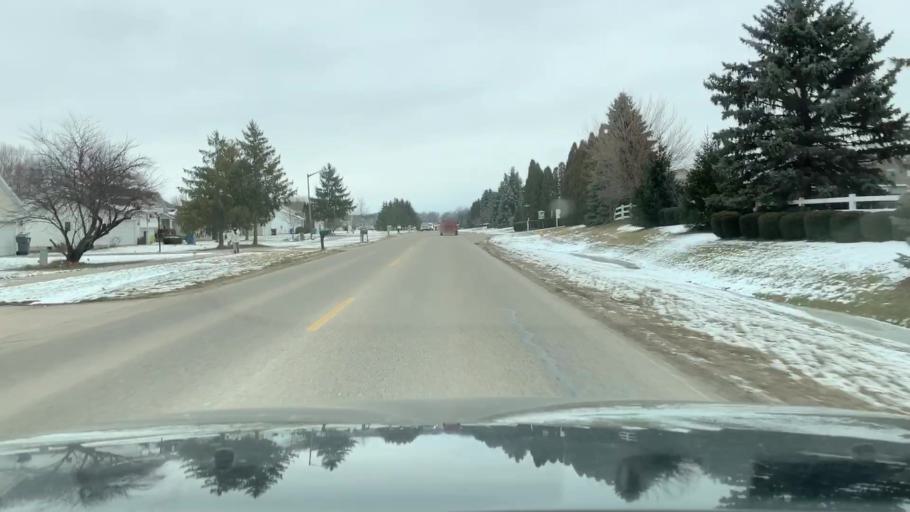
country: US
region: Michigan
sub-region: Ottawa County
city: Zeeland
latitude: 42.7912
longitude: -86.0381
